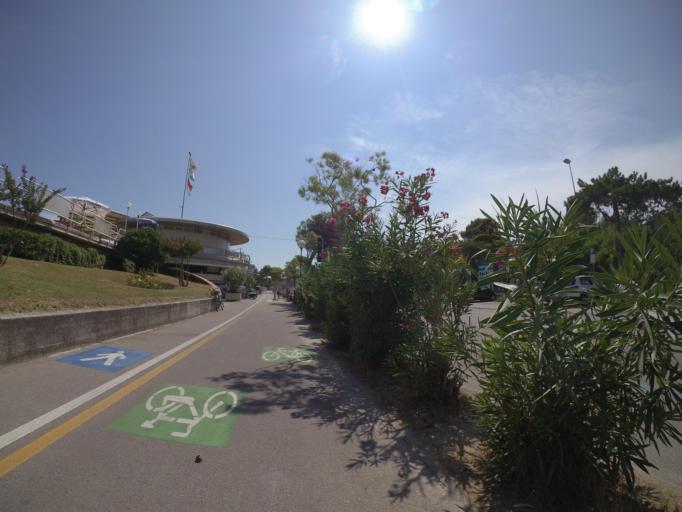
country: IT
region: Friuli Venezia Giulia
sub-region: Provincia di Udine
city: Lignano Sabbiadoro
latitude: 45.6634
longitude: 13.1088
